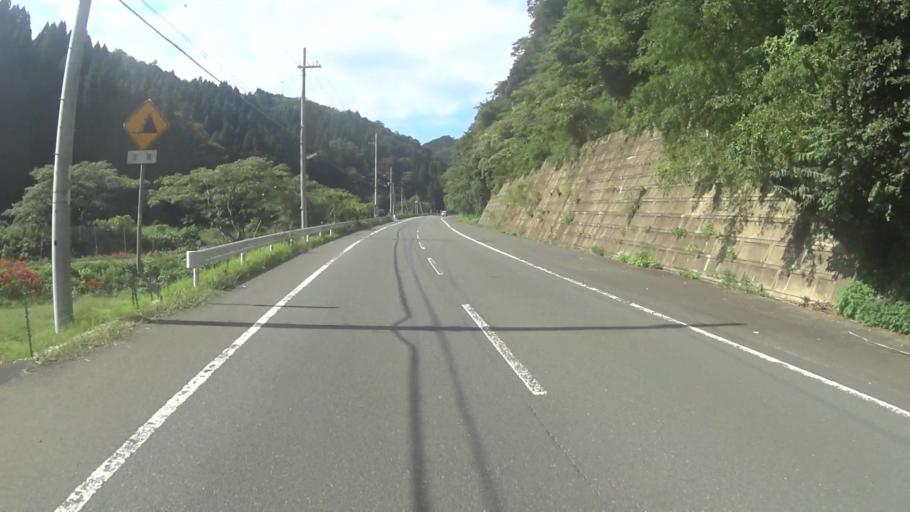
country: JP
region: Kyoto
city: Miyazu
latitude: 35.7331
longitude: 135.2575
